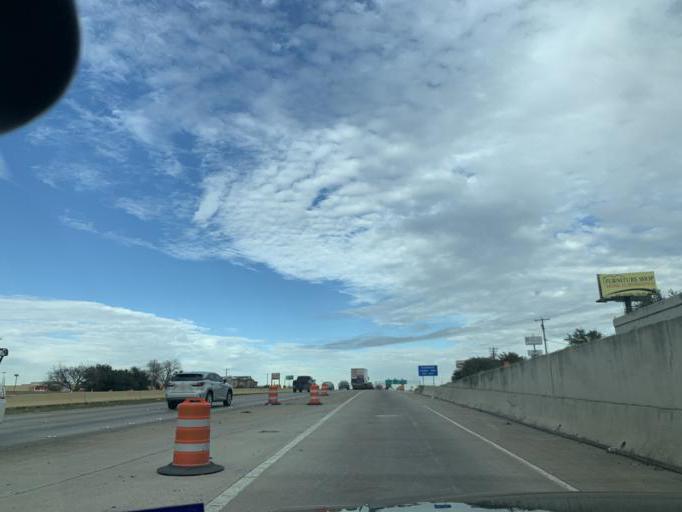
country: US
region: Texas
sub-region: Dallas County
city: Duncanville
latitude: 32.6429
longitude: -96.8893
